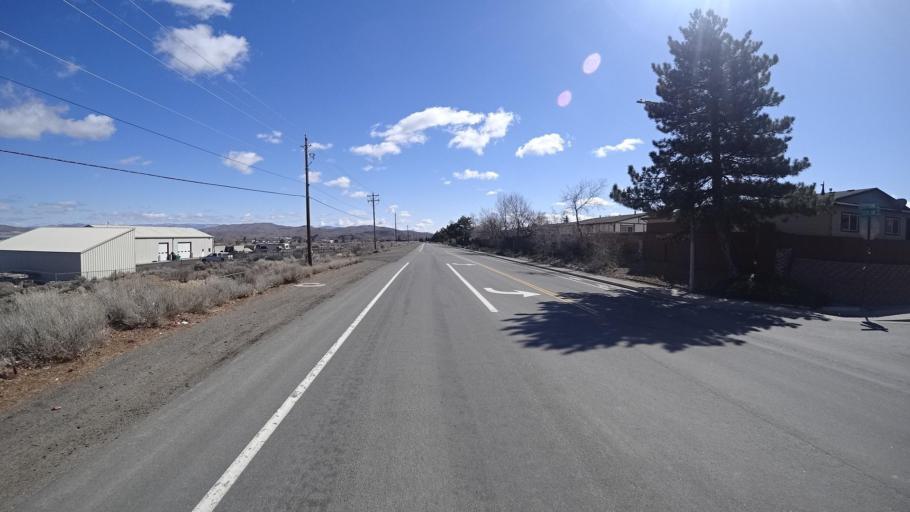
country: US
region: Nevada
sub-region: Washoe County
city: Lemmon Valley
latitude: 39.6257
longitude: -119.8925
